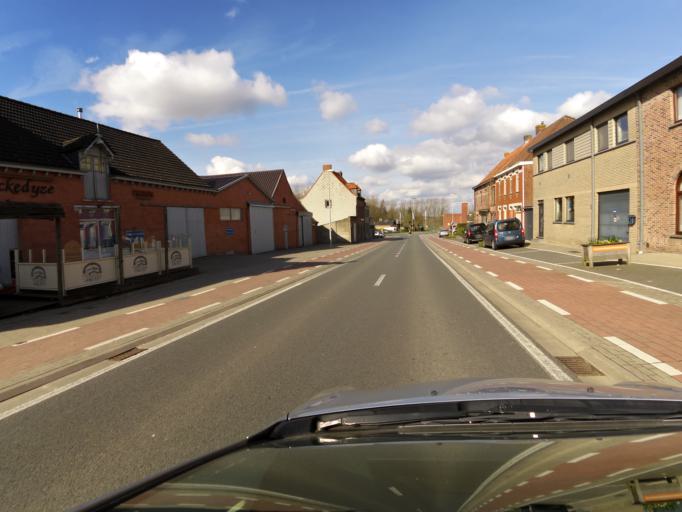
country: FR
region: Nord-Pas-de-Calais
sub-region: Departement du Nord
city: Nieppe
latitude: 50.7815
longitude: 2.8303
